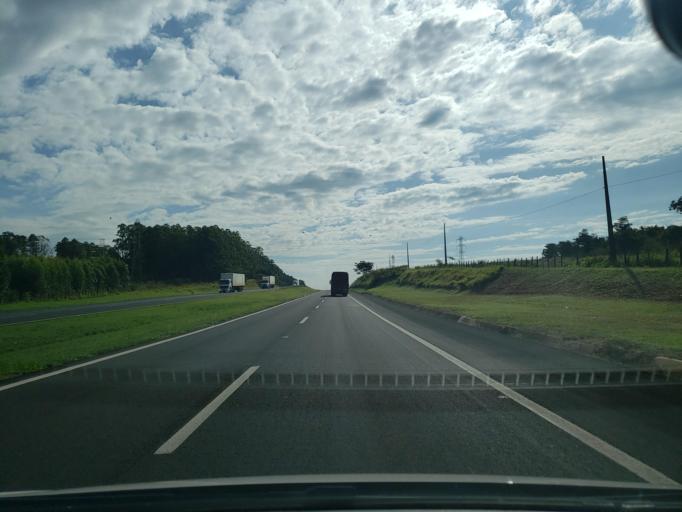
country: BR
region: Sao Paulo
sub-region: Lins
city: Lins
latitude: -21.6722
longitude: -49.7799
